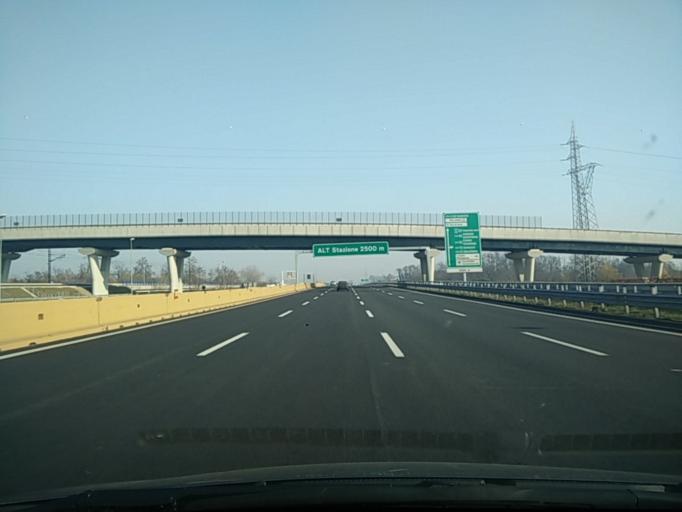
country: IT
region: Lombardy
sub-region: Citta metropolitana di Milano
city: Cornaredo
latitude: 45.5088
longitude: 9.0291
